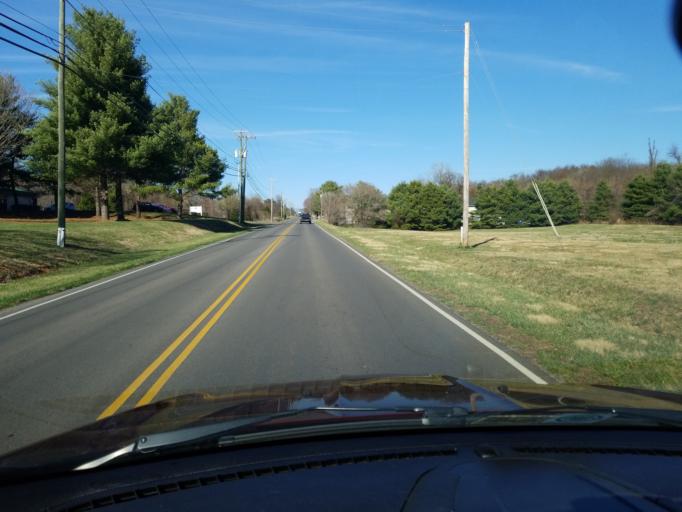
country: US
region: Virginia
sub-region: Roanoke County
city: Hollins
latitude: 37.3421
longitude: -79.9251
